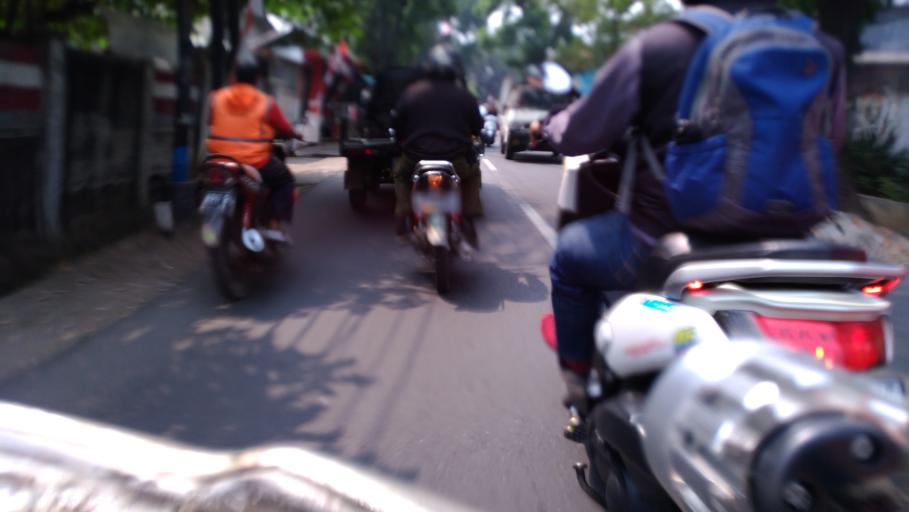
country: ID
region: West Java
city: Depok
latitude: -6.3402
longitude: 106.8767
